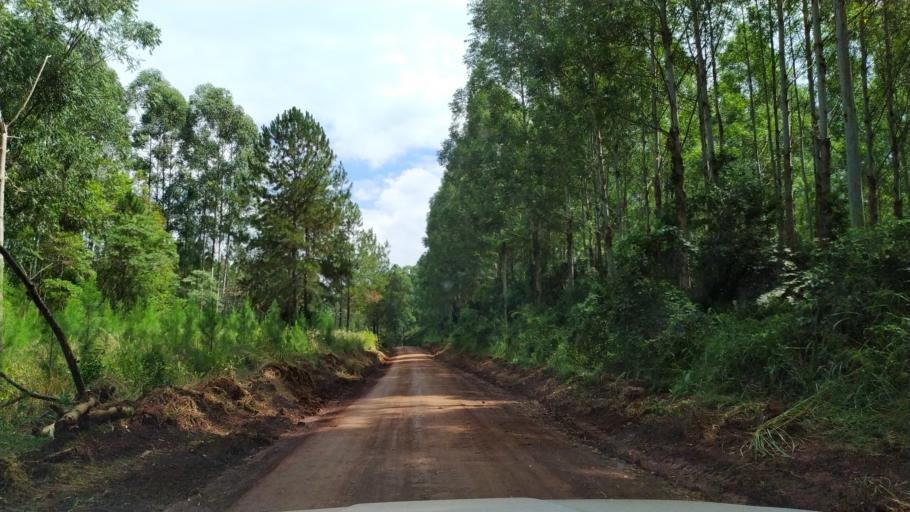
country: AR
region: Misiones
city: Puerto Piray
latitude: -26.5324
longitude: -54.6289
